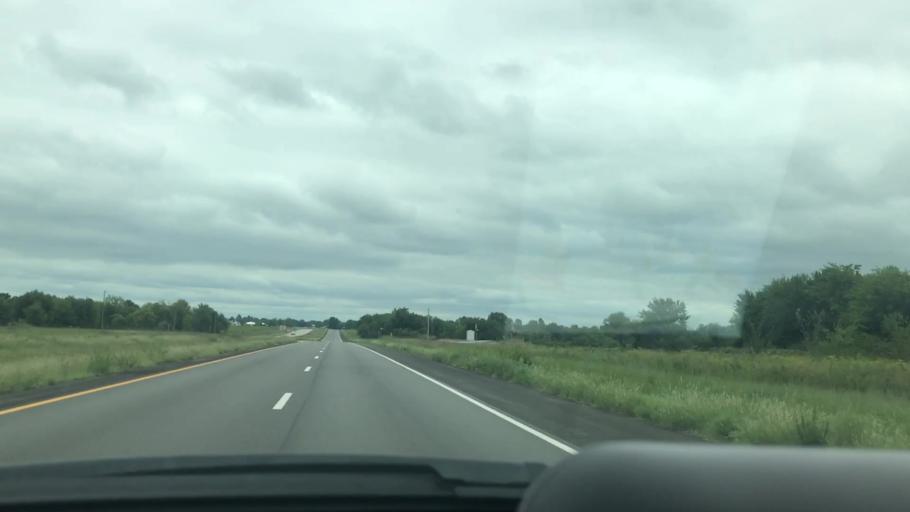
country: US
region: Oklahoma
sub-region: Mayes County
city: Pryor
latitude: 36.4653
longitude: -95.2607
